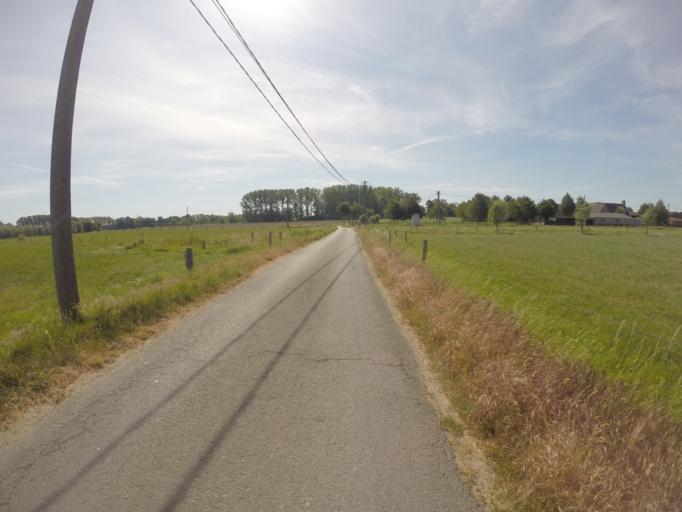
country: BE
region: Flanders
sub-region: Provincie West-Vlaanderen
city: Beernem
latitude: 51.1847
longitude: 3.3180
